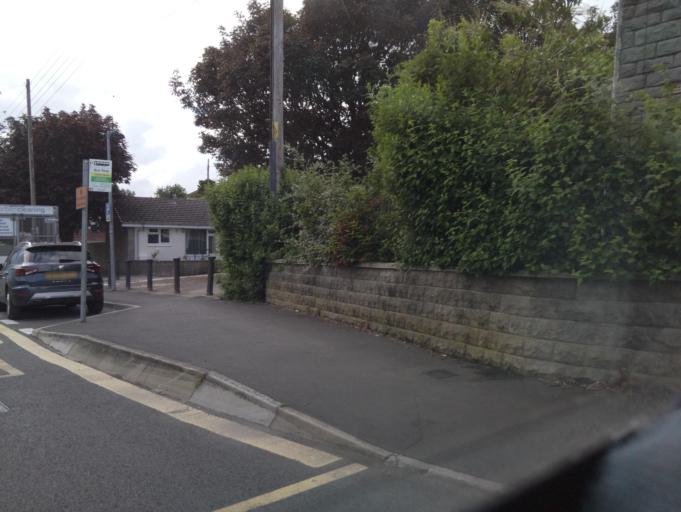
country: GB
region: England
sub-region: South Gloucestershire
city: Kingswood
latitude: 51.4514
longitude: -2.5089
